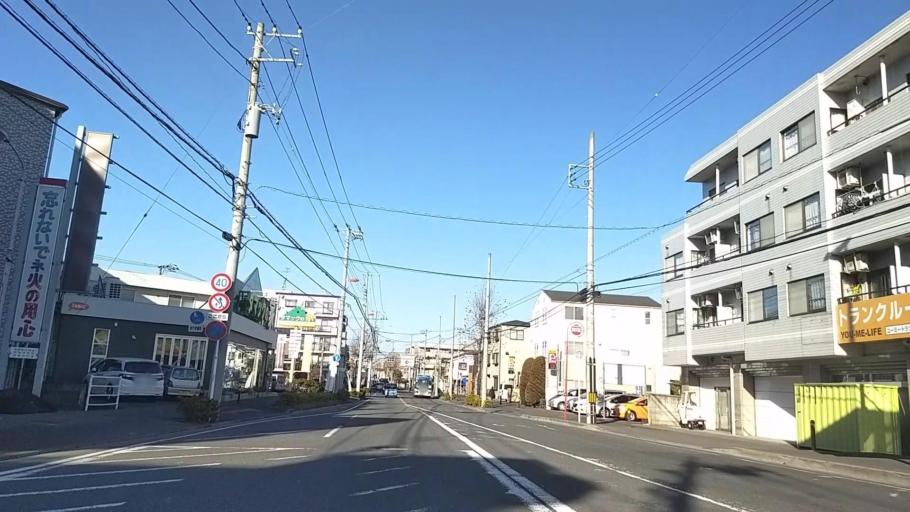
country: JP
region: Tokyo
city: Chofugaoka
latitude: 35.6182
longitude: 139.5574
